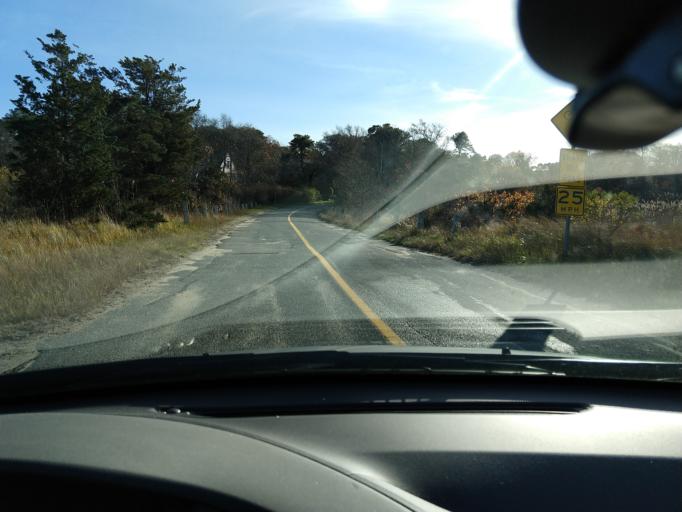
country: US
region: Massachusetts
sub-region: Barnstable County
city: Orleans
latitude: 41.7829
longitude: -70.0334
